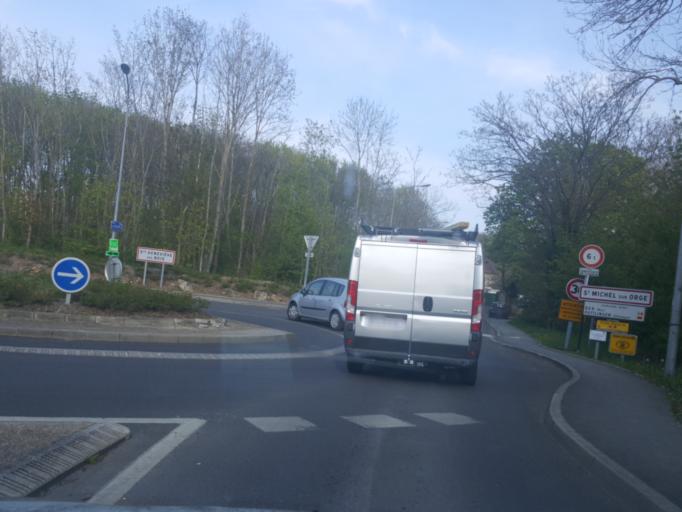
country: FR
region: Ile-de-France
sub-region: Departement de l'Essonne
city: Longpont-sur-Orge
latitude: 48.6446
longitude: 2.2999
